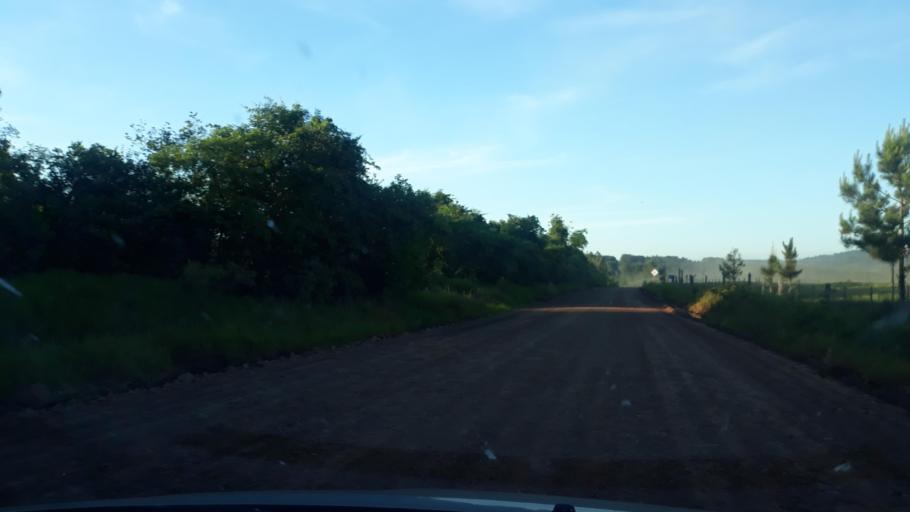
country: AR
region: Misiones
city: Ruiz de Montoya
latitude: -27.0498
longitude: -55.0041
